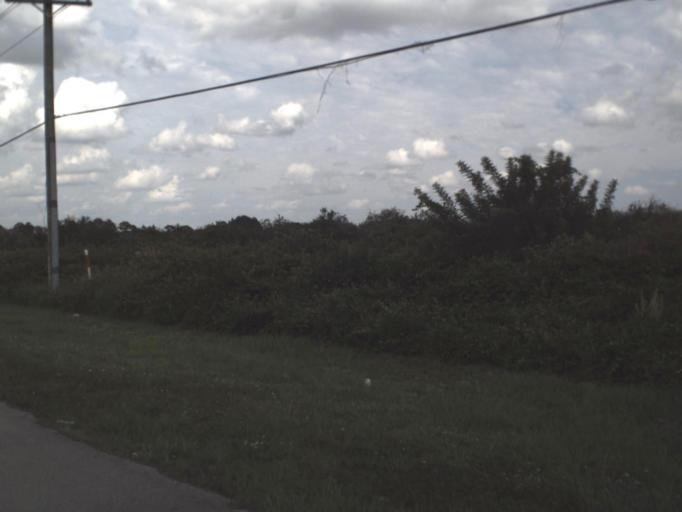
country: US
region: Florida
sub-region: Hendry County
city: LaBelle
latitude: 26.7266
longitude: -81.4376
